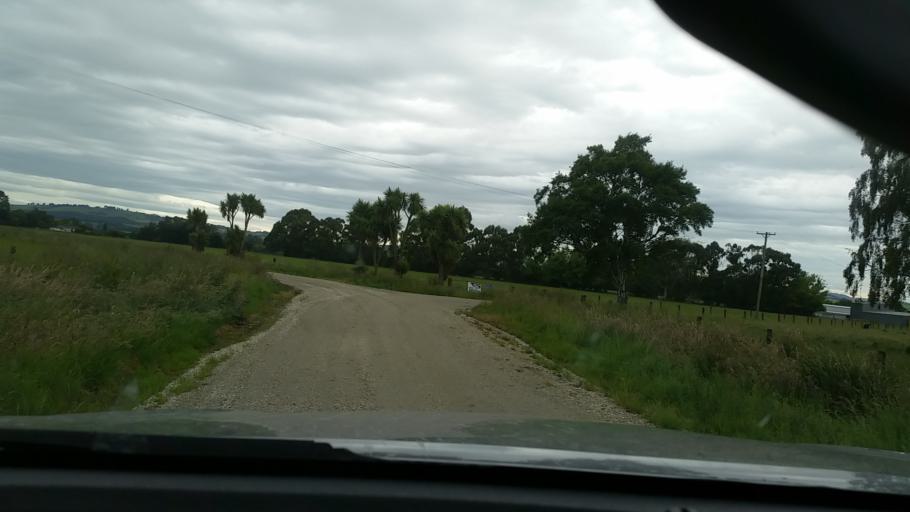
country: NZ
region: Southland
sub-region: Gore District
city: Gore
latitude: -46.2889
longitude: 168.8217
